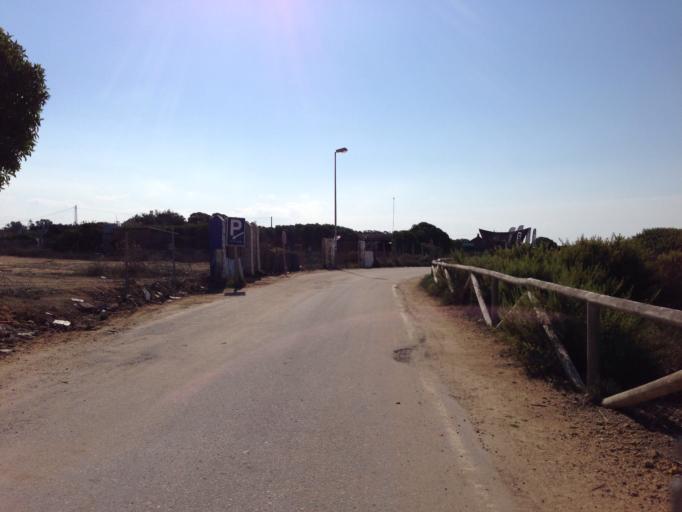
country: ES
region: Andalusia
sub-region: Provincia de Cadiz
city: Conil de la Frontera
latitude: 36.2183
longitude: -6.0608
